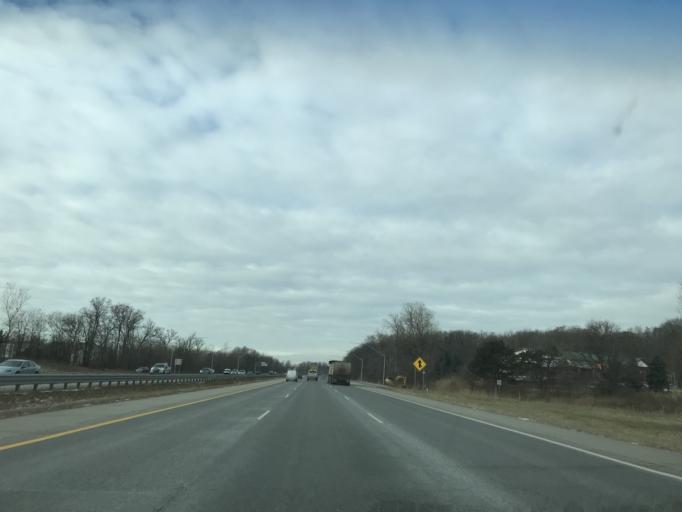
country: US
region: Michigan
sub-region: Oakland County
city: Pontiac
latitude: 42.7049
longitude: -83.3101
